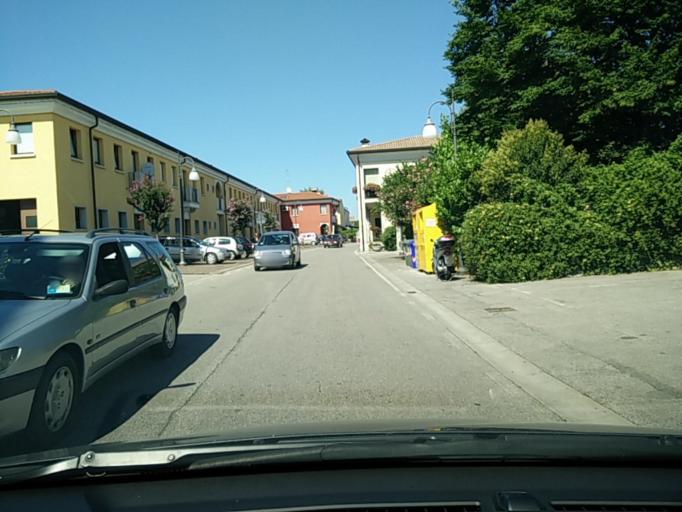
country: IT
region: Veneto
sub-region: Provincia di Venezia
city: Concordia Sagittaria
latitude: 45.7566
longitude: 12.8417
